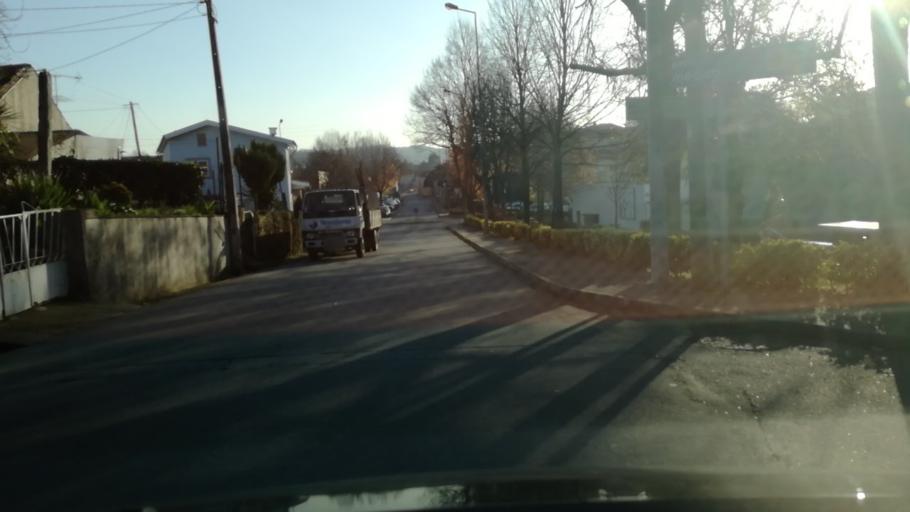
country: PT
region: Braga
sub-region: Vila Nova de Famalicao
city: Ferreiros
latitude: 41.3526
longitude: -8.5292
